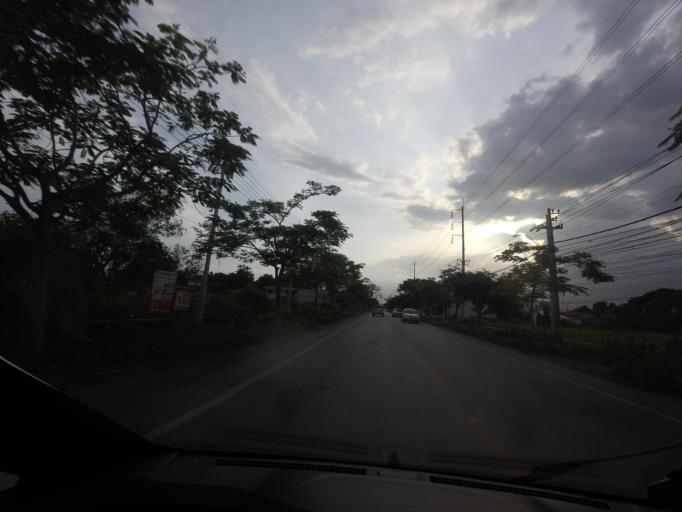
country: TH
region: Bangkok
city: Nong Chok
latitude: 13.8548
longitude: 100.8122
